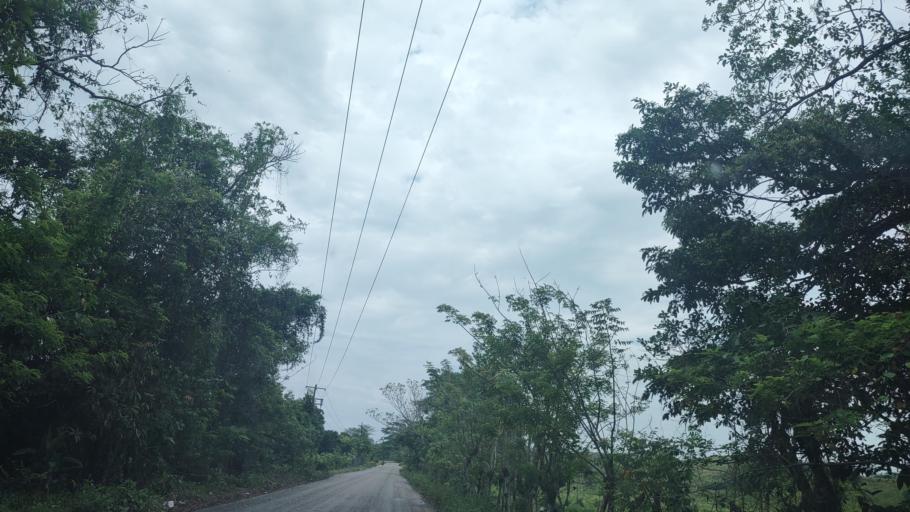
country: MX
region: Tabasco
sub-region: Huimanguillo
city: Francisco Rueda
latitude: 17.5359
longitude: -94.1269
